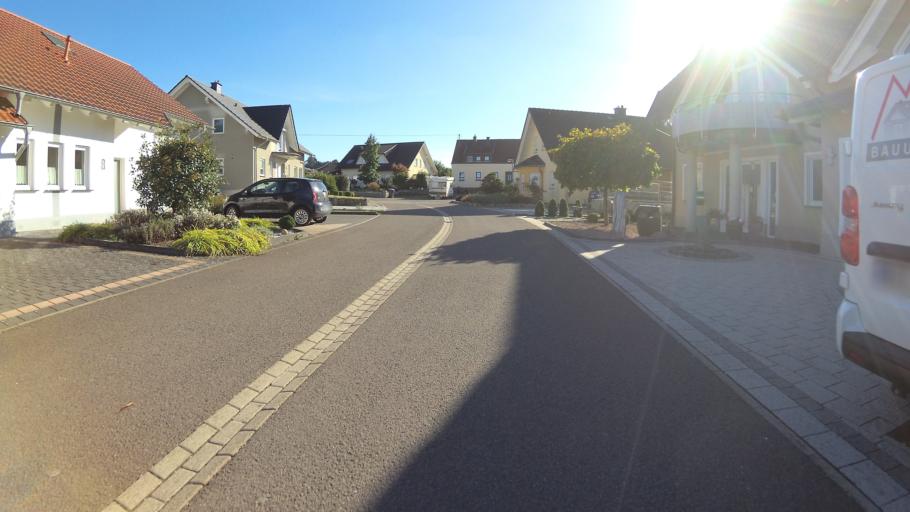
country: DE
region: Saarland
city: Eppelborn
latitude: 49.4081
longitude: 6.9394
